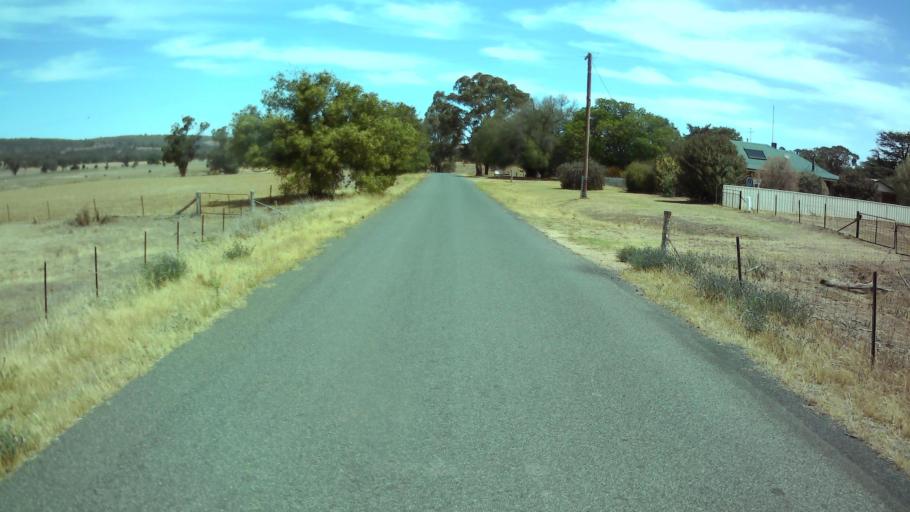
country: AU
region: New South Wales
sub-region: Weddin
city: Grenfell
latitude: -33.8333
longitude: 148.1739
